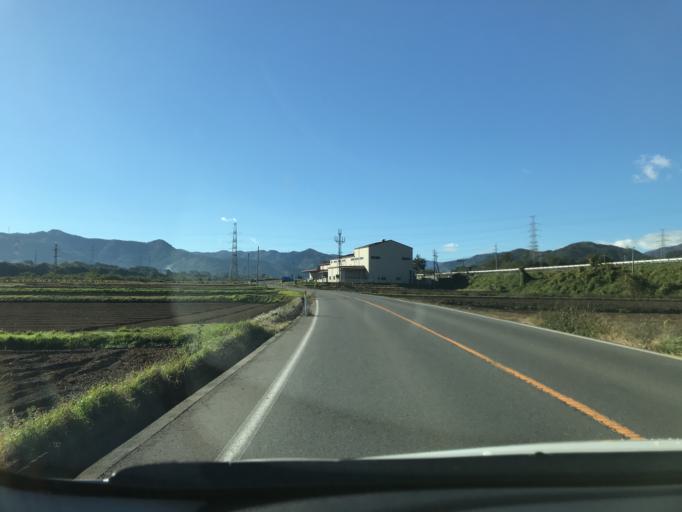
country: JP
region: Nagano
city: Shiojiri
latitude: 36.1301
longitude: 137.9257
